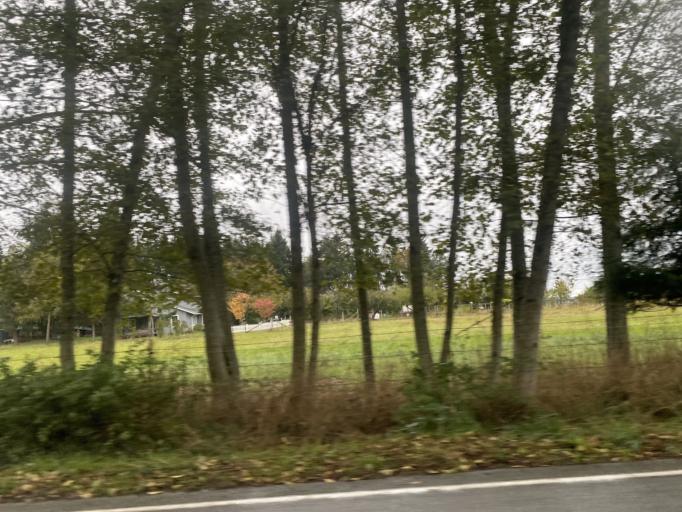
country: US
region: Washington
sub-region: Island County
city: Freeland
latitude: 48.0803
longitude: -122.4859
